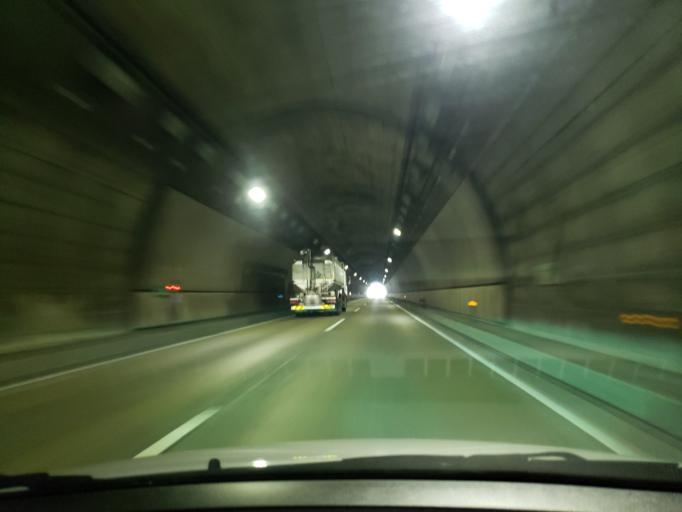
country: JP
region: Hyogo
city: Tatsunocho-tominaga
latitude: 34.8472
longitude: 134.5775
